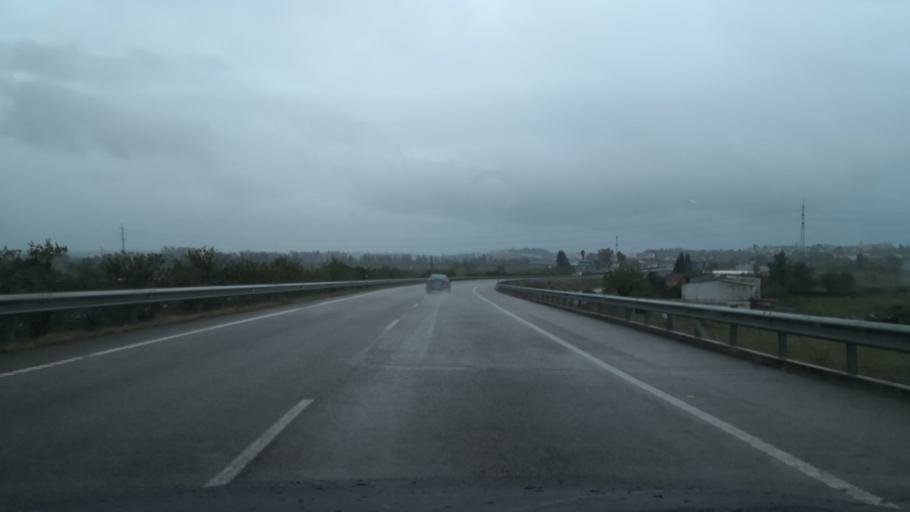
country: ES
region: Extremadura
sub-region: Provincia de Badajoz
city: Badajoz
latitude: 38.9121
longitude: -6.9636
